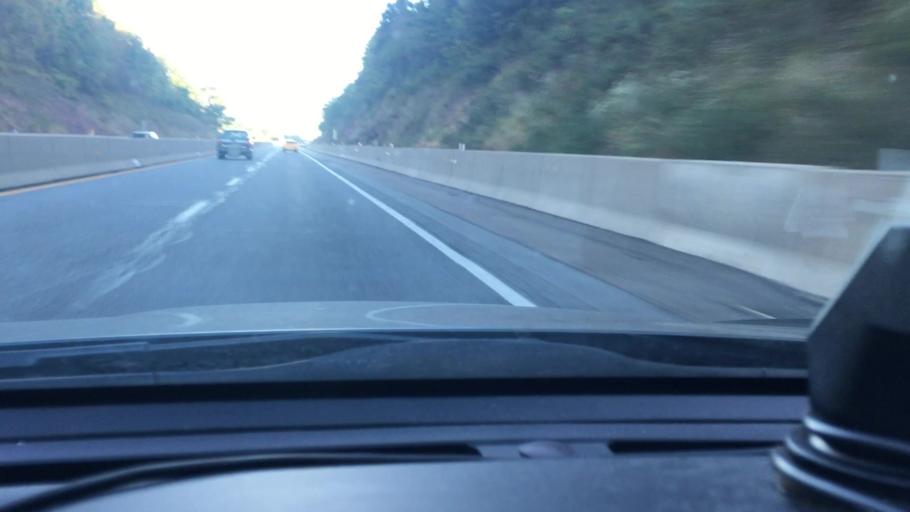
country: US
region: Pennsylvania
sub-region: Carbon County
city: Towamensing Trails
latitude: 40.9281
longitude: -75.6445
